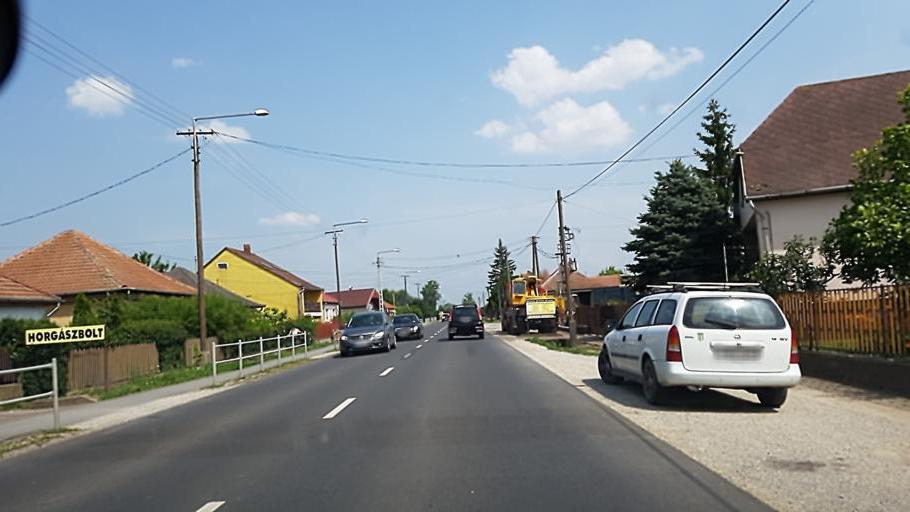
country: HU
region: Heves
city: Besenyotelek
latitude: 47.6938
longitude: 20.4392
